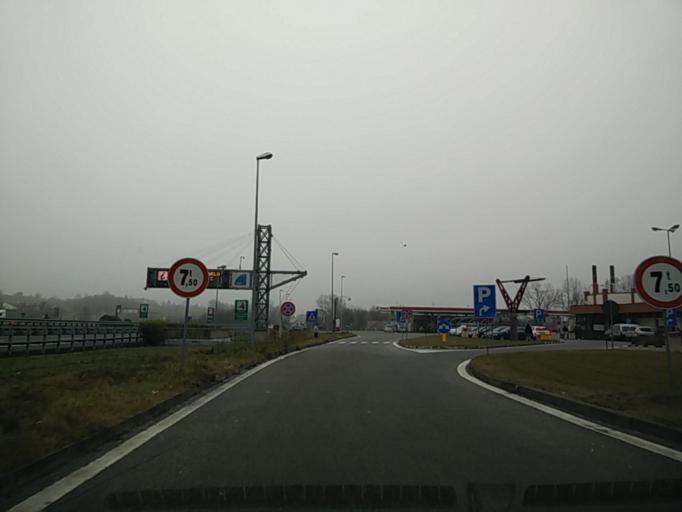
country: IT
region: Piedmont
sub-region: Provincia di Asti
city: Cerro Tanaro
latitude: 44.9040
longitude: 8.3628
